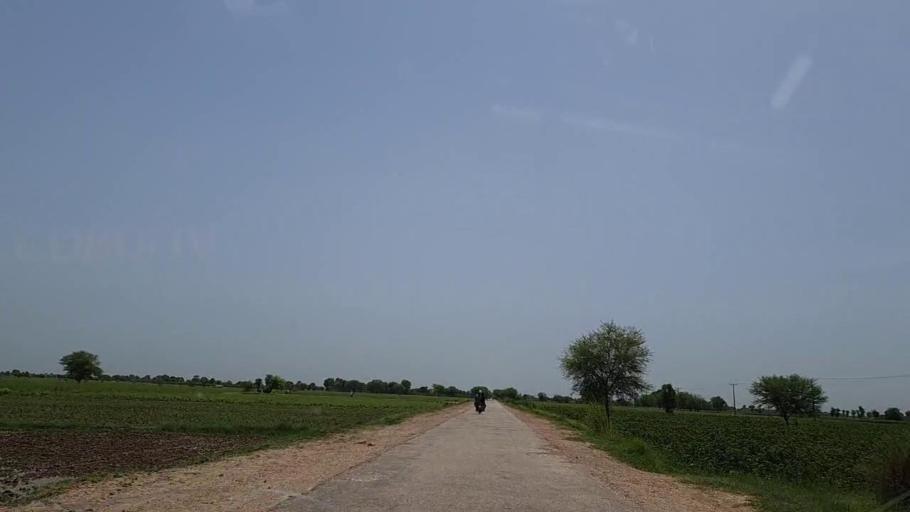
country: PK
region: Sindh
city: Tharu Shah
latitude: 26.9613
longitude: 68.0610
